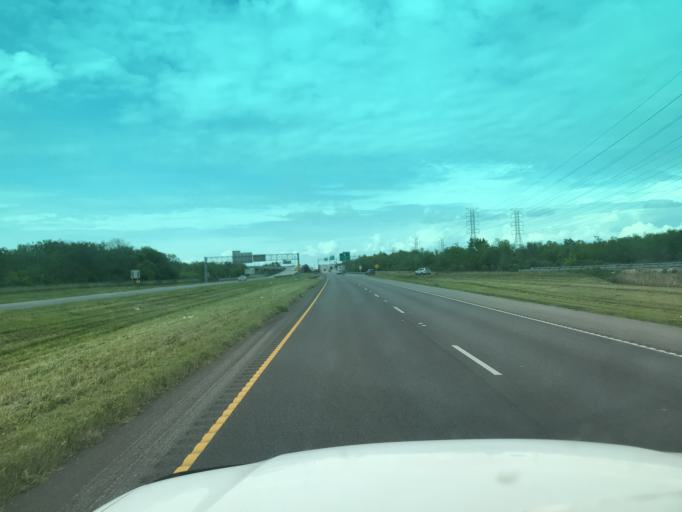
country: US
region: Louisiana
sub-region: Saint Bernard Parish
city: Chalmette
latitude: 30.0187
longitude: -89.9394
